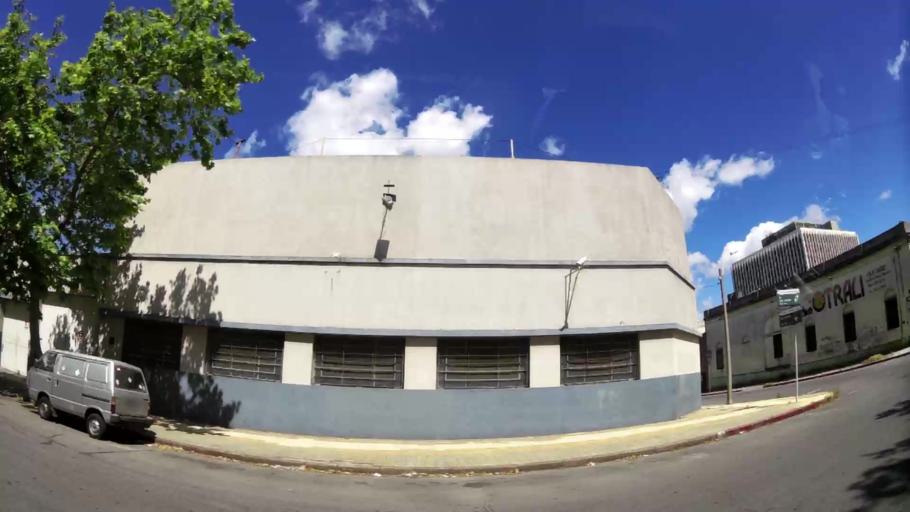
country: UY
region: Montevideo
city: Montevideo
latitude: -34.8869
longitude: -56.1934
